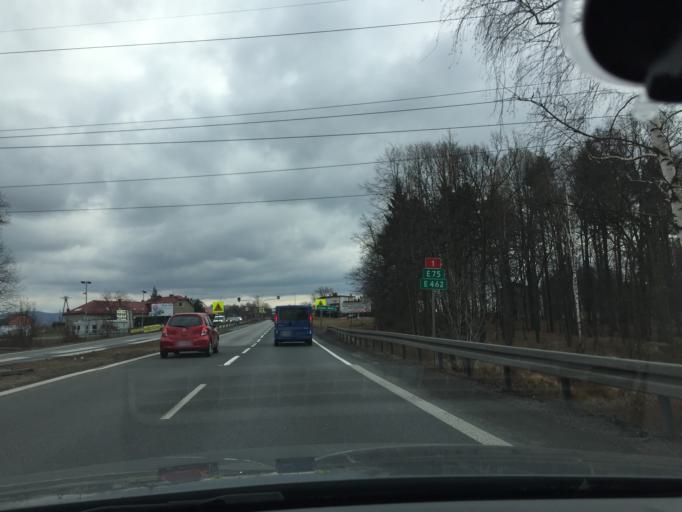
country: PL
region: Silesian Voivodeship
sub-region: Powiat bielski
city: Mazancowice
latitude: 49.8652
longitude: 19.0123
